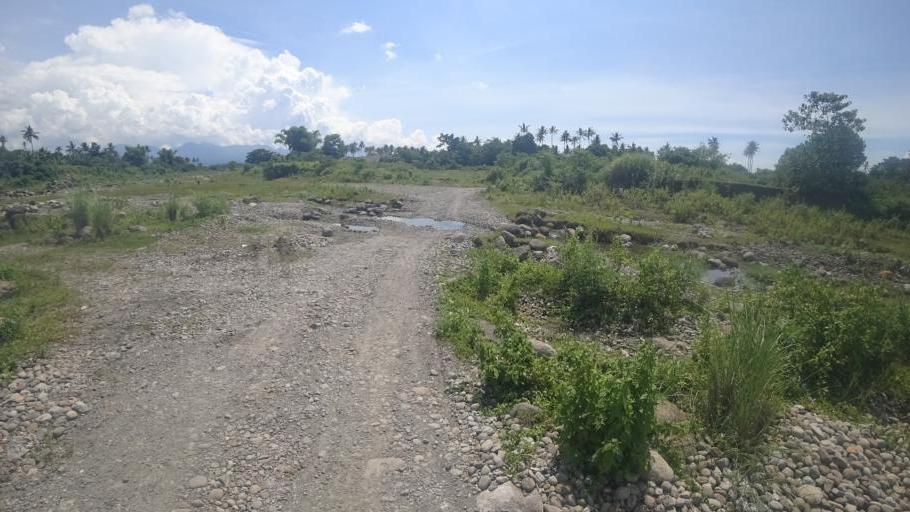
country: PH
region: Eastern Visayas
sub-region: Province of Leyte
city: Jaro
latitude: 11.1996
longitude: 124.8088
